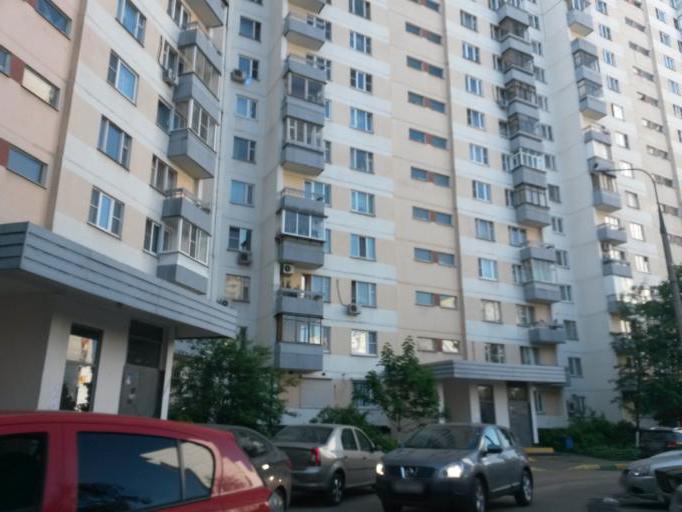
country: RU
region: Moscow
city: Mar'ino
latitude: 55.6488
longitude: 37.7417
